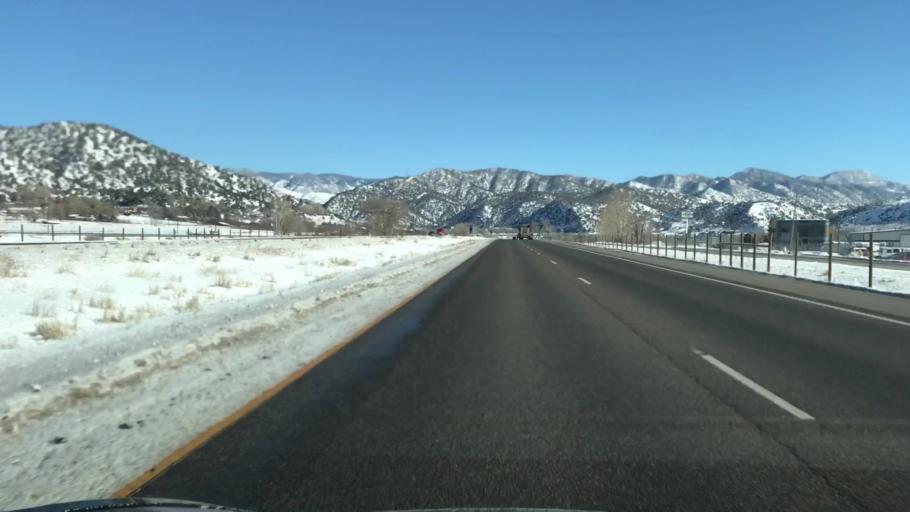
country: US
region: Colorado
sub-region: Garfield County
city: New Castle
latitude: 39.5551
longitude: -107.5724
